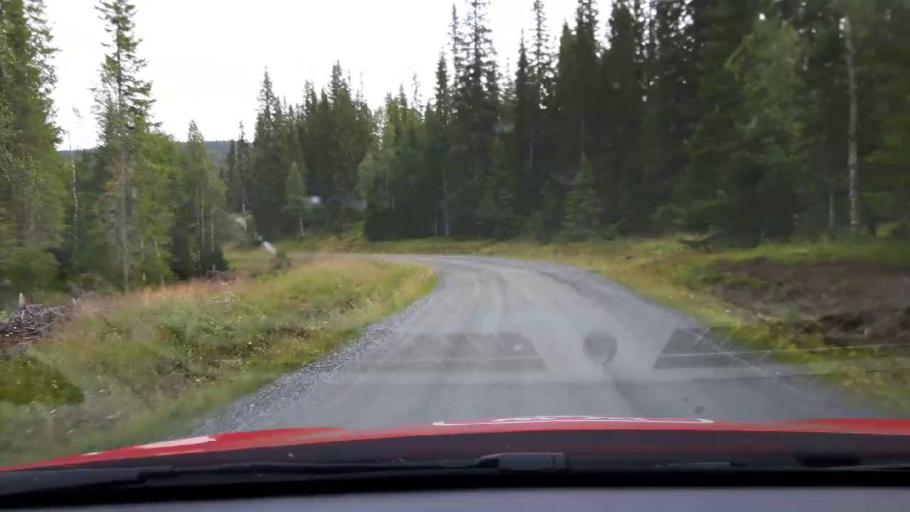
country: SE
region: Jaemtland
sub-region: Are Kommun
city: Are
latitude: 63.7731
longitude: 13.0750
